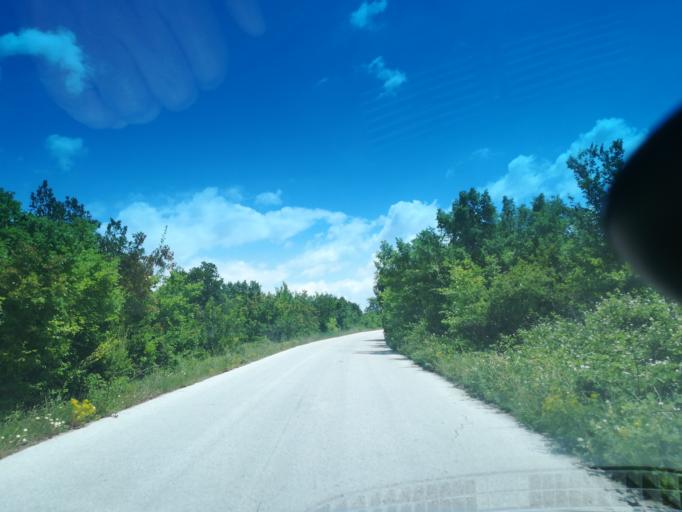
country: BG
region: Khaskovo
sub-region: Obshtina Mineralni Bani
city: Mineralni Bani
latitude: 41.9859
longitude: 25.2446
